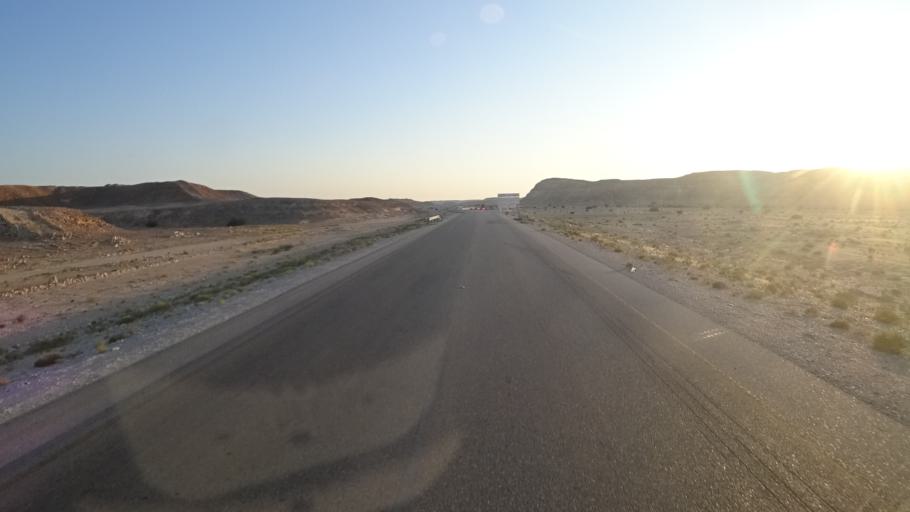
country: OM
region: Zufar
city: Salalah
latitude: 17.5254
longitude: 53.3793
